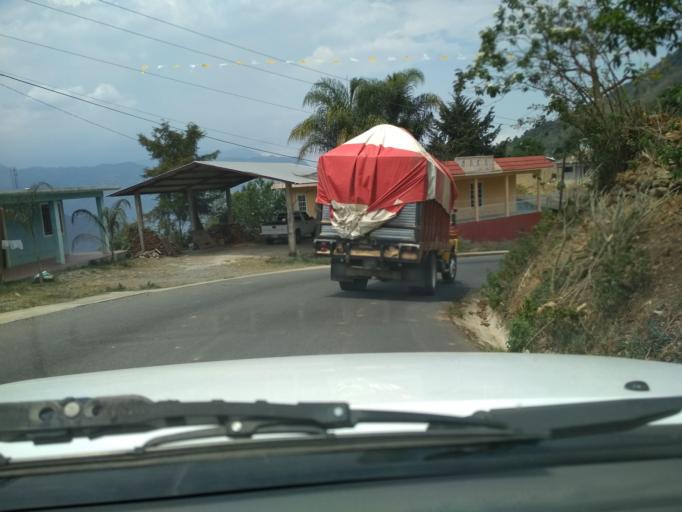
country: MX
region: Veracruz
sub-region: Acultzingo
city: Acatla
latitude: 18.7525
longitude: -97.1953
